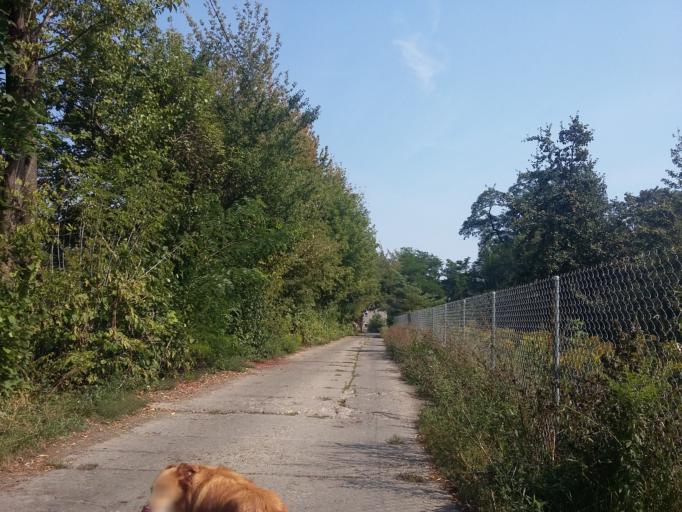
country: PL
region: Lodz Voivodeship
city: Lodz
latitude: 51.7420
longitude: 19.4129
